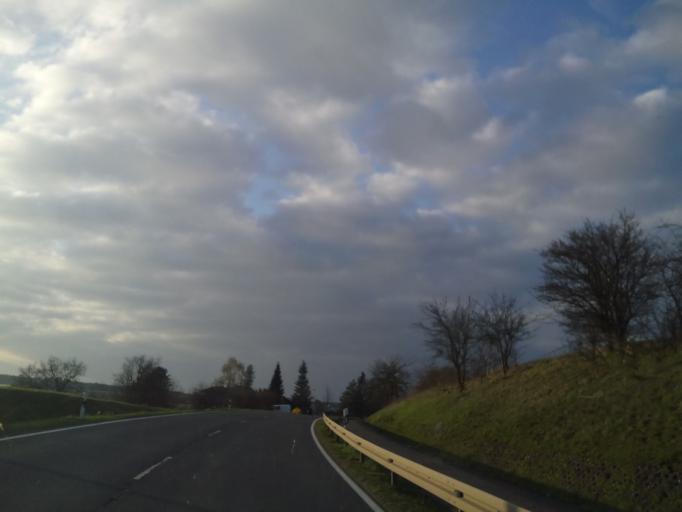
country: DE
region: Bavaria
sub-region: Regierungsbezirk Unterfranken
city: Maroldsweisach
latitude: 50.1889
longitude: 10.6635
